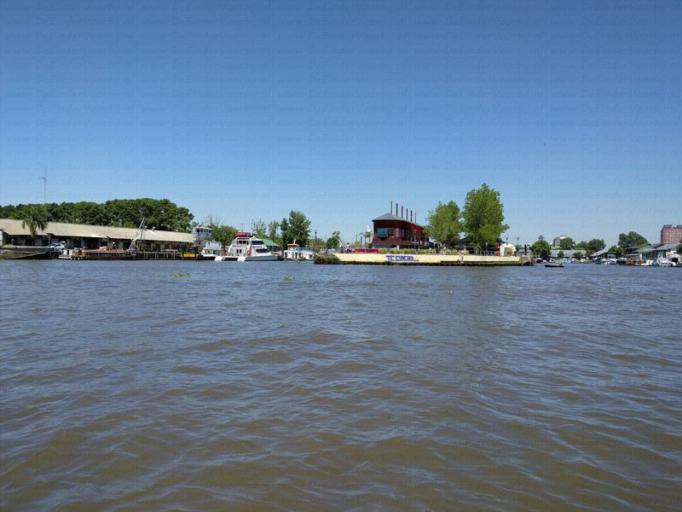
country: AR
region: Buenos Aires
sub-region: Partido de Tigre
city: Tigre
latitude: -34.4165
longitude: -58.5690
